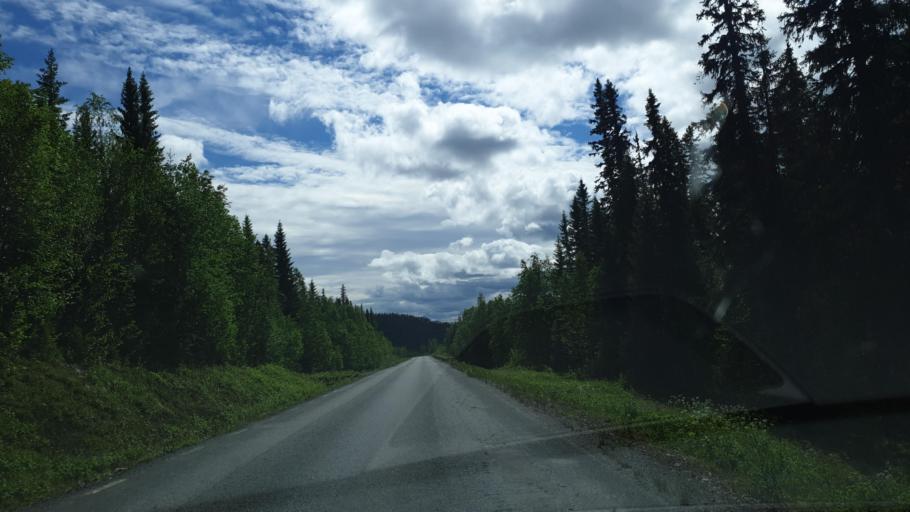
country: SE
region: Vaesterbotten
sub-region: Vilhelmina Kommun
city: Sjoberg
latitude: 64.9740
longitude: 15.8551
